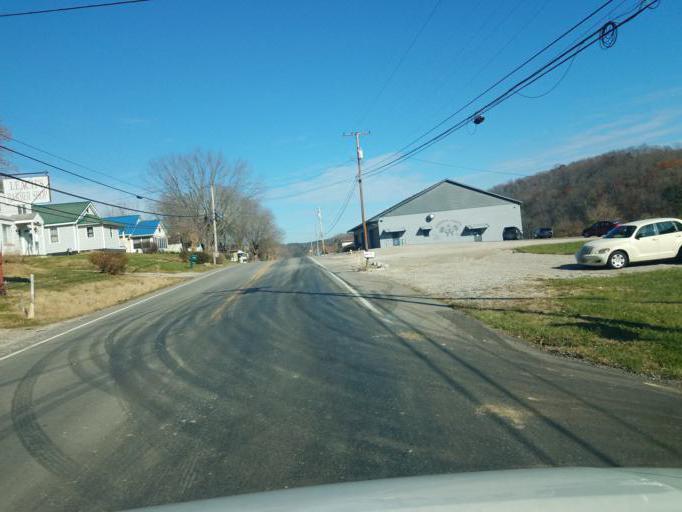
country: US
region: Ohio
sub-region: Scioto County
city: Rosemount
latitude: 38.8280
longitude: -82.9258
